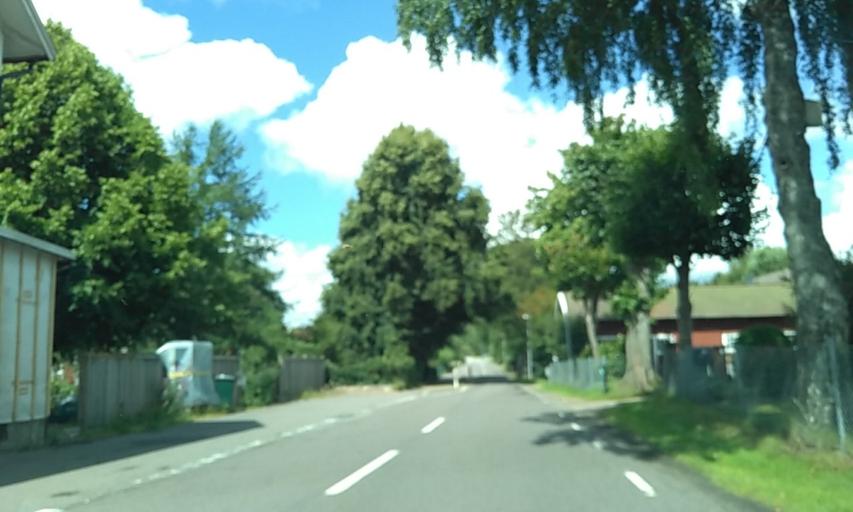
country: SE
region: Vaestra Goetaland
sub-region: Lerums Kommun
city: Grabo
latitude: 57.9154
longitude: 12.3686
